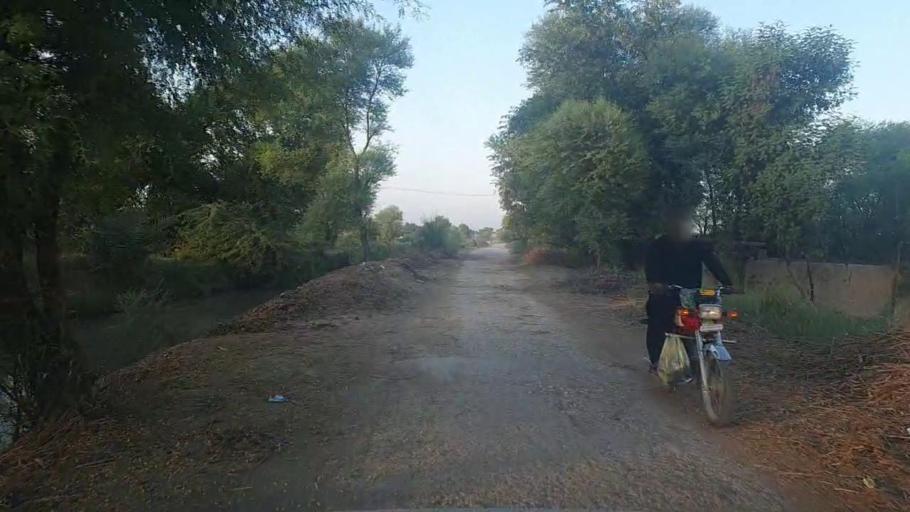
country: PK
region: Sindh
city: Khairpur
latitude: 28.0843
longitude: 69.7183
